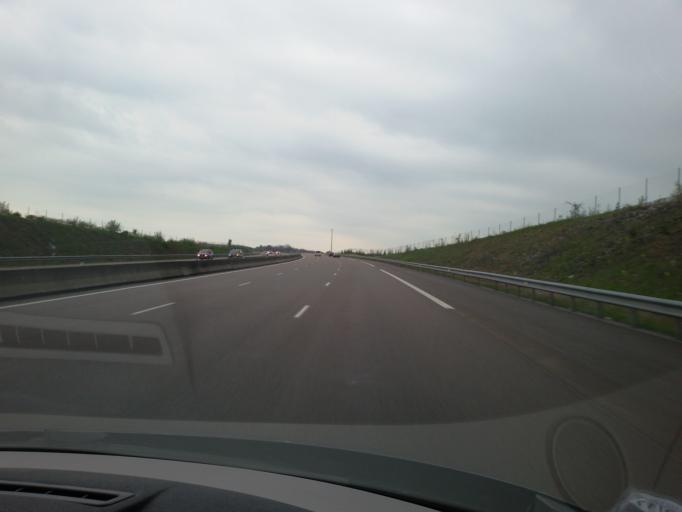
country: FR
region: Champagne-Ardenne
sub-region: Departement de la Haute-Marne
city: Langres
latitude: 47.8392
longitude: 5.2317
